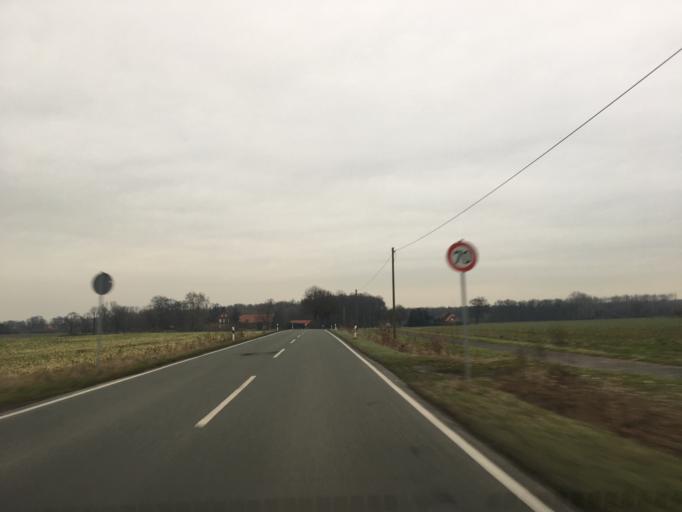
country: DE
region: North Rhine-Westphalia
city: Selm
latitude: 51.7307
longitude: 7.4634
